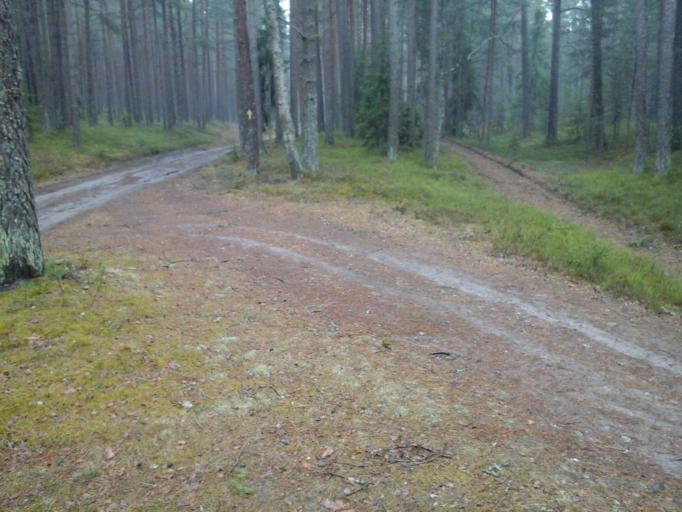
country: LV
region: Salacgrivas
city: Salacgriva
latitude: 57.7100
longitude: 24.3518
